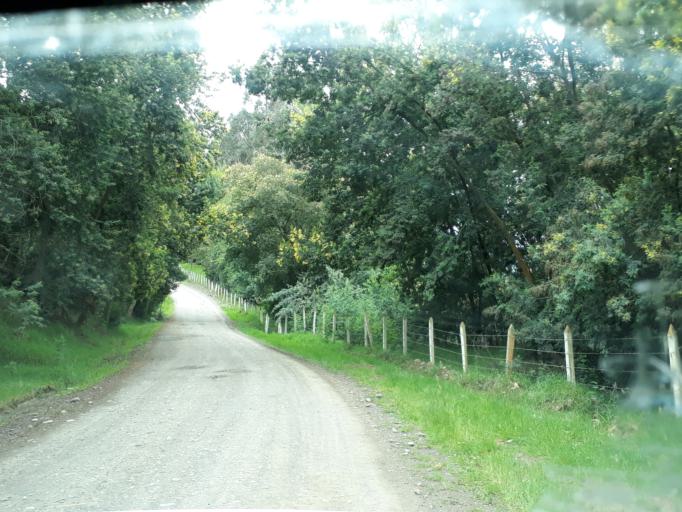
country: CO
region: Cundinamarca
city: La Mesa
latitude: 5.2984
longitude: -73.9055
